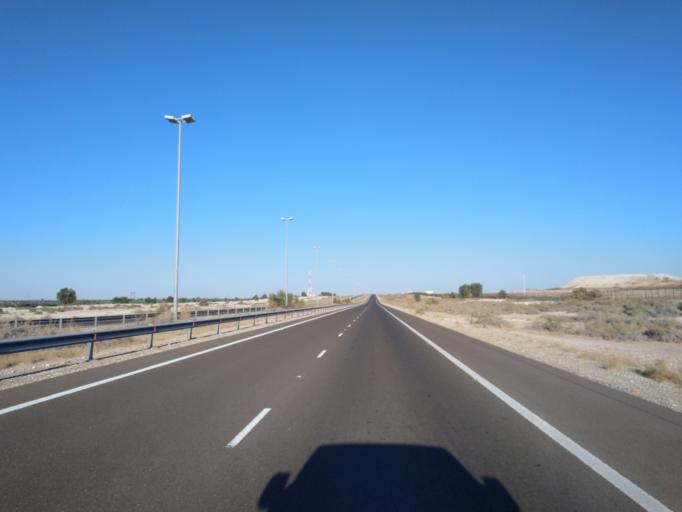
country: OM
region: Al Buraimi
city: Al Buraymi
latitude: 24.5317
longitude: 55.5741
